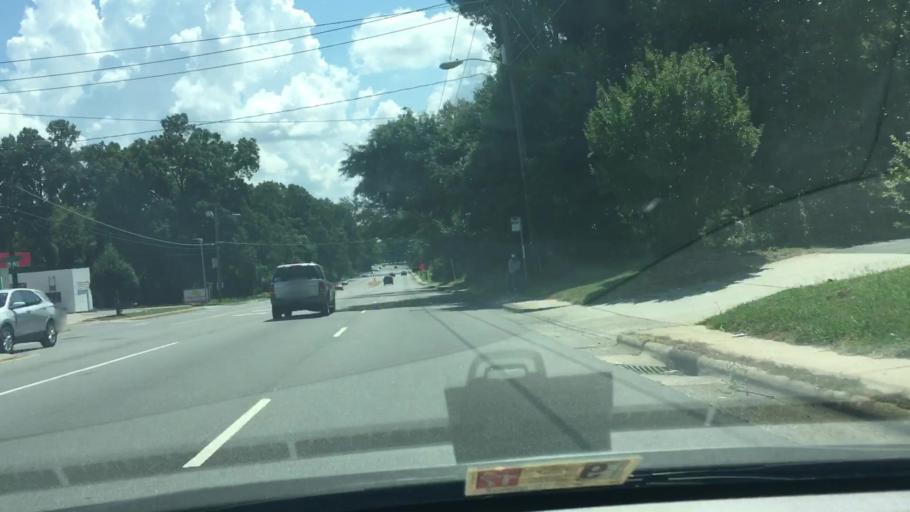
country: US
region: North Carolina
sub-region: Mecklenburg County
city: Charlotte
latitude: 35.2659
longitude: -80.7951
